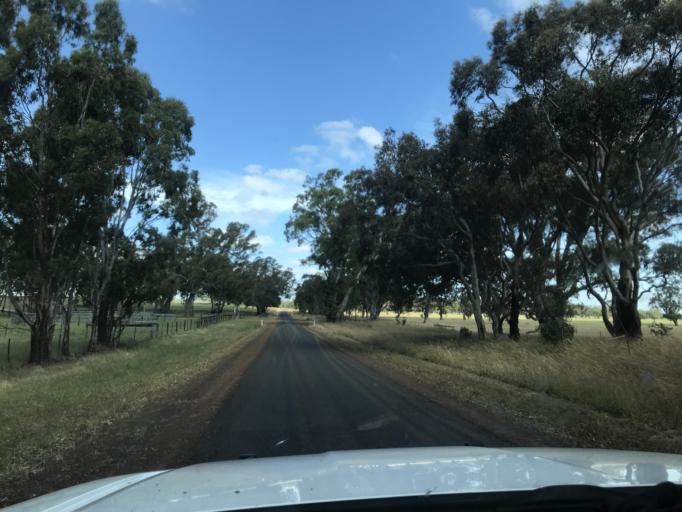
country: AU
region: South Australia
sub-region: Naracoorte and Lucindale
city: Naracoorte
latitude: -36.8632
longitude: 141.1691
